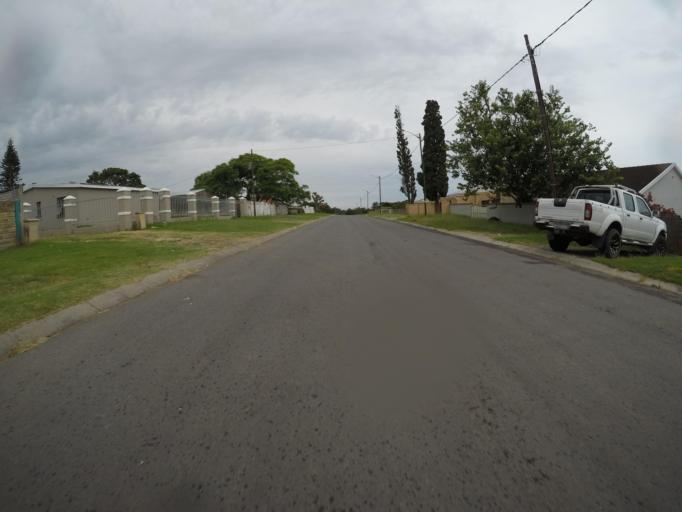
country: ZA
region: Eastern Cape
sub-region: Buffalo City Metropolitan Municipality
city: East London
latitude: -32.9668
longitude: 27.8331
